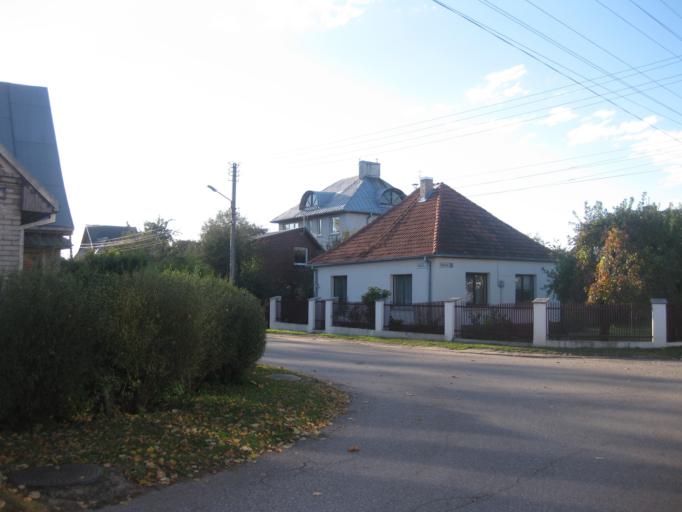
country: LT
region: Kauno apskritis
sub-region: Kaunas
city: Aleksotas
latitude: 54.8877
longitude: 23.8985
